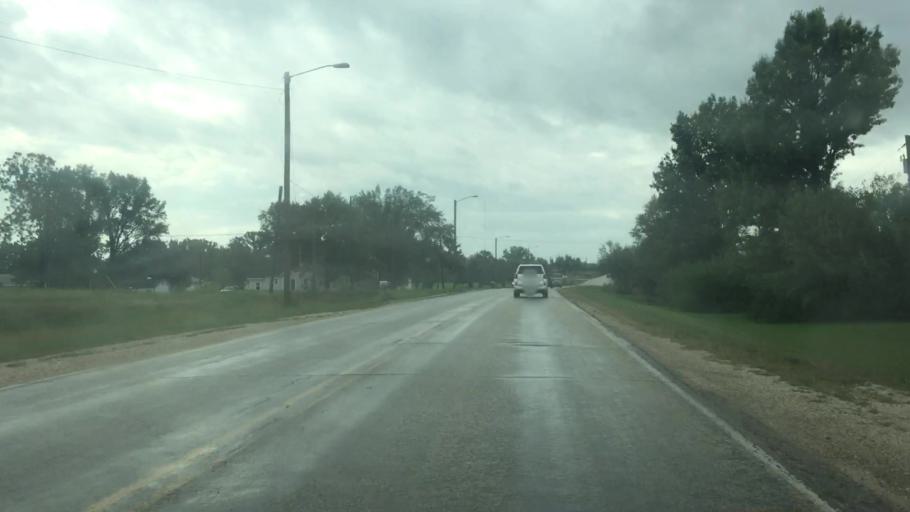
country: US
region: Kansas
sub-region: Allen County
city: Iola
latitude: 37.9036
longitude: -95.4096
